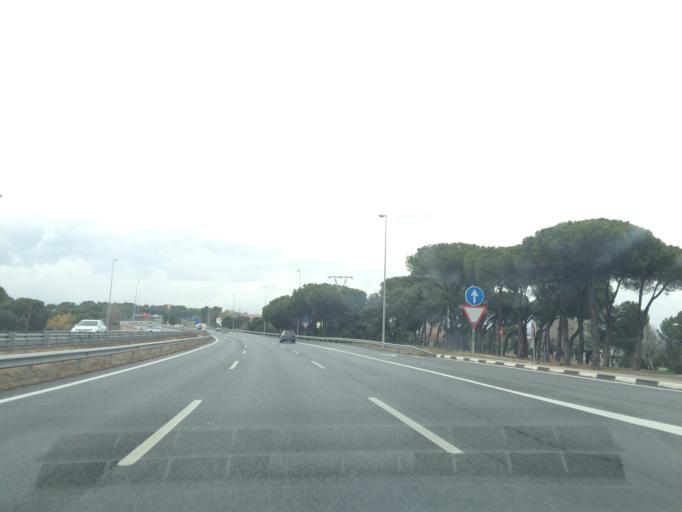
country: ES
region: Madrid
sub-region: Provincia de Madrid
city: Tres Cantos
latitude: 40.5853
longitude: -3.7068
